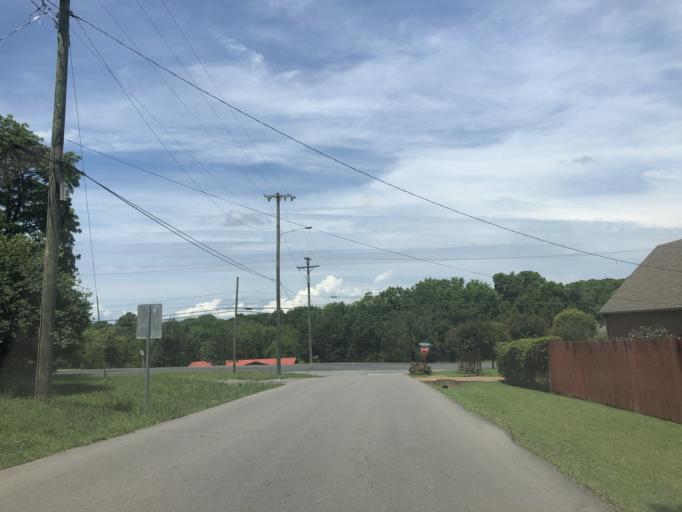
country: US
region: Tennessee
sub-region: Davidson County
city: Lakewood
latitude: 36.2581
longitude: -86.6844
